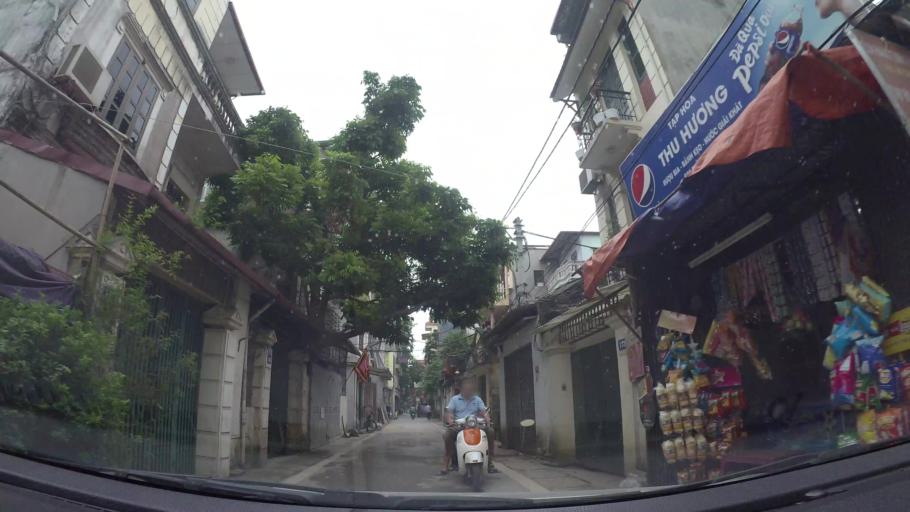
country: VN
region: Ha Noi
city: Tay Ho
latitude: 21.0682
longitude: 105.8351
